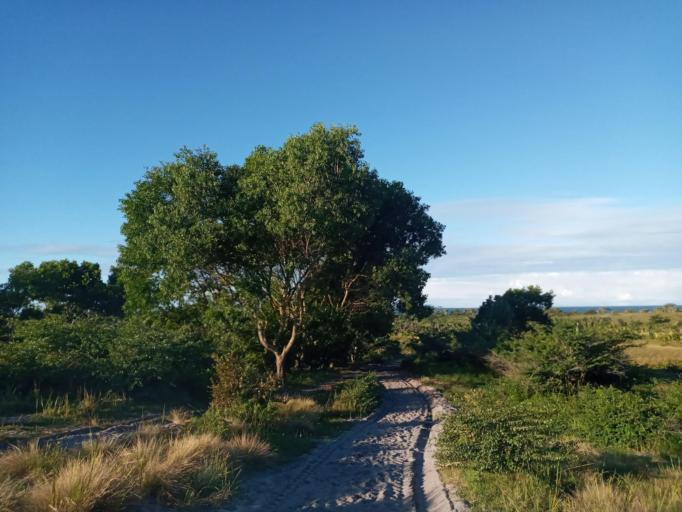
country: MG
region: Anosy
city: Fort Dauphin
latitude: -24.4315
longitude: 47.2997
